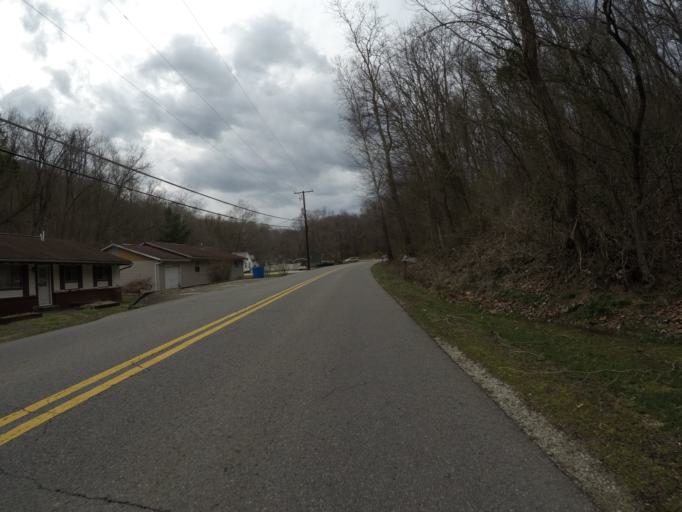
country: US
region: Ohio
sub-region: Lawrence County
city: Burlington
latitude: 38.4279
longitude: -82.5182
